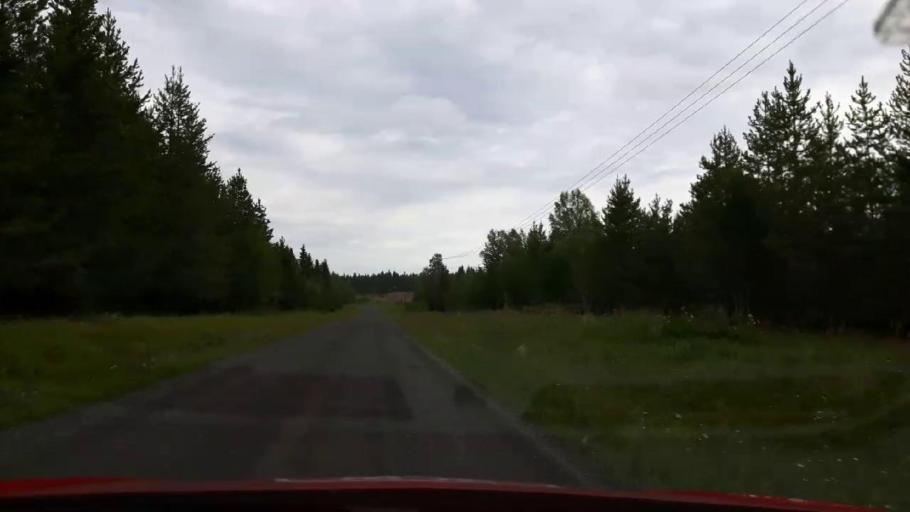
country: SE
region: Jaemtland
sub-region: Stroemsunds Kommun
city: Stroemsund
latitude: 63.4757
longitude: 15.2956
